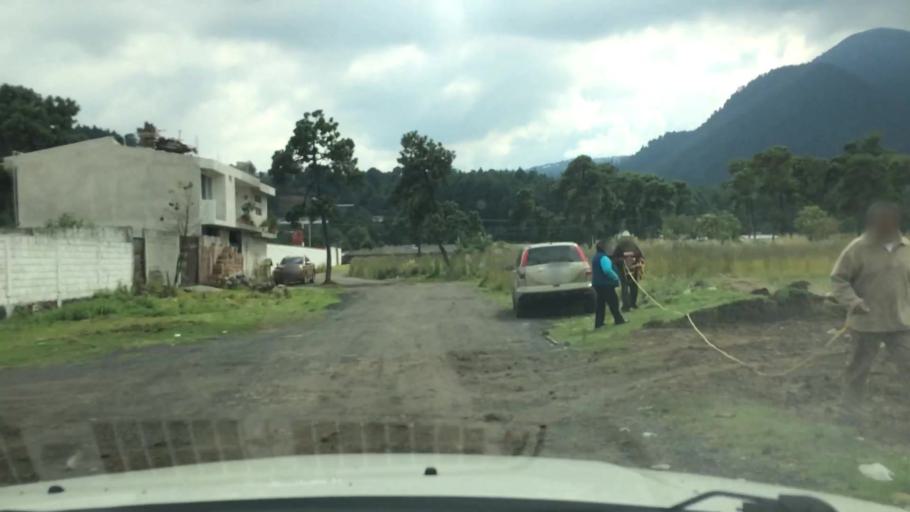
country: MX
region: Mexico City
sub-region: Tlalpan
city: Lomas de Tepemecatl
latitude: 19.2338
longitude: -99.2225
